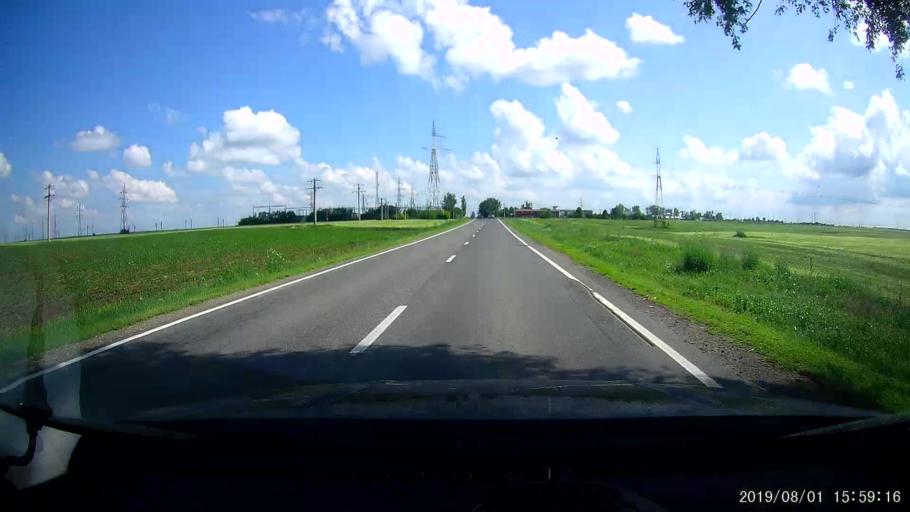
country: RO
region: Ialomita
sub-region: Comuna Slobozia
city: Slobozia
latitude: 44.5523
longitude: 27.3824
